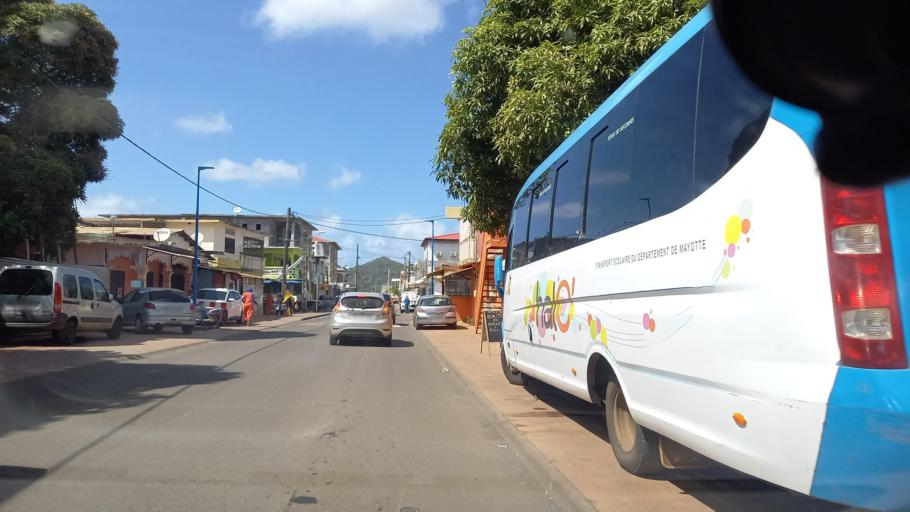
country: YT
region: Mamoudzou
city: Mamoudzou
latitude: -12.8017
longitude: 45.2114
